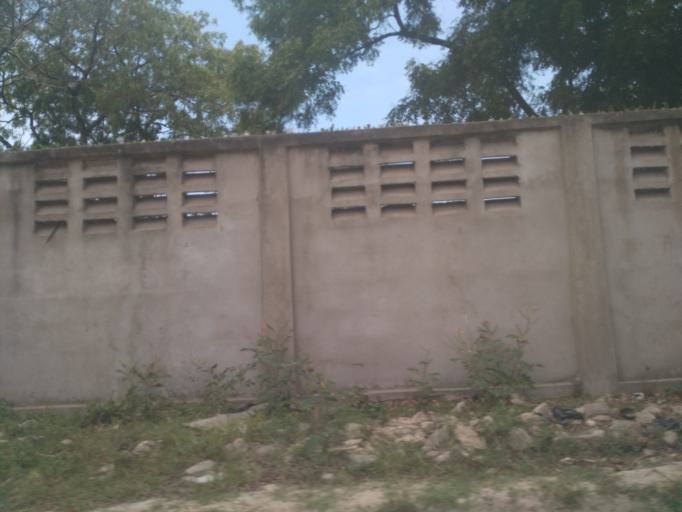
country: TZ
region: Dar es Salaam
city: Dar es Salaam
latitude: -6.8372
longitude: 39.2843
